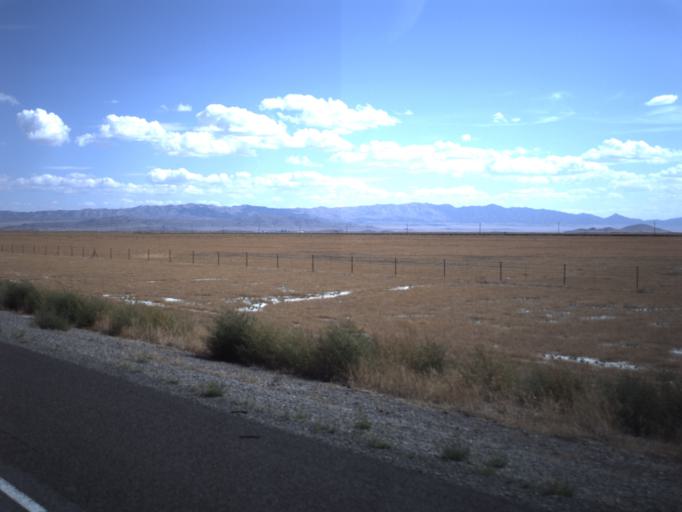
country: US
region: Utah
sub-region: Tooele County
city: Grantsville
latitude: 40.7261
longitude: -113.2292
